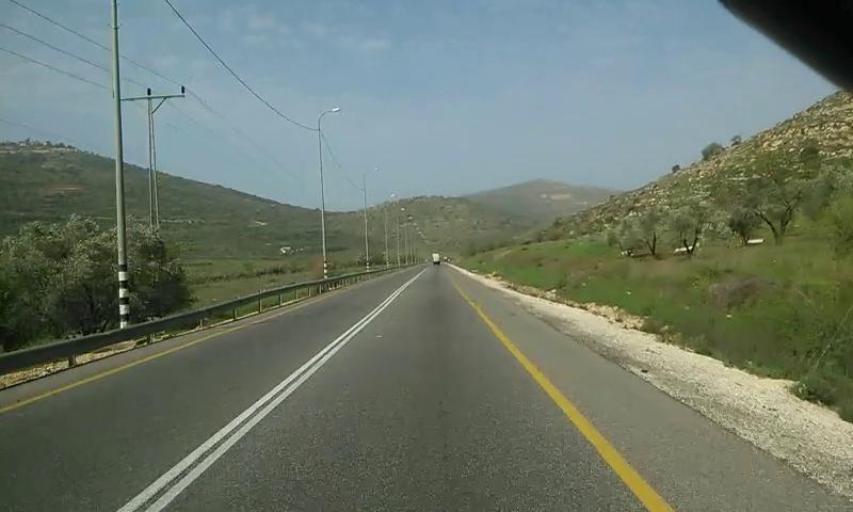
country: PS
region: West Bank
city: Al Lubban ash Sharqiyah
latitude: 32.0627
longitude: 35.2513
